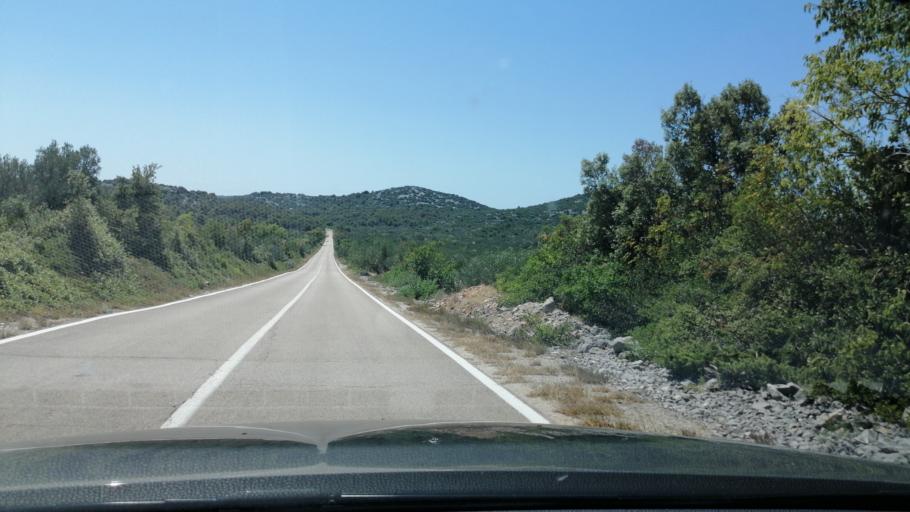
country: HR
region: Sibensko-Kniniska
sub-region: Grad Sibenik
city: Pirovac
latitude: 43.8523
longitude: 15.6879
